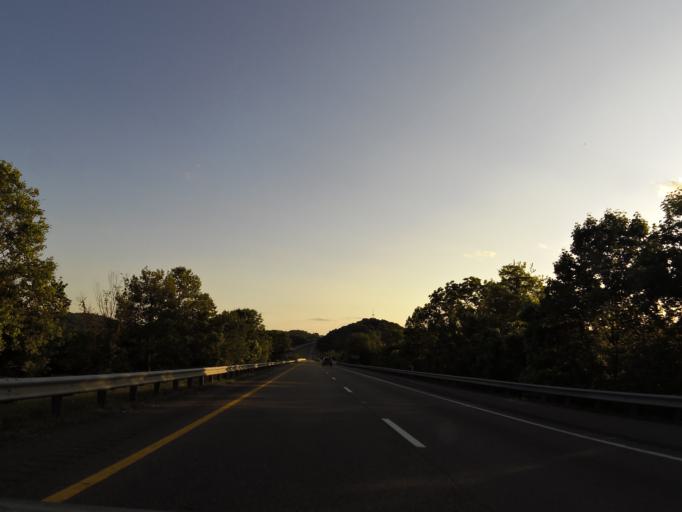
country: US
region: Tennessee
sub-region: Sullivan County
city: Colonial Heights
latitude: 36.4861
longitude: -82.4736
